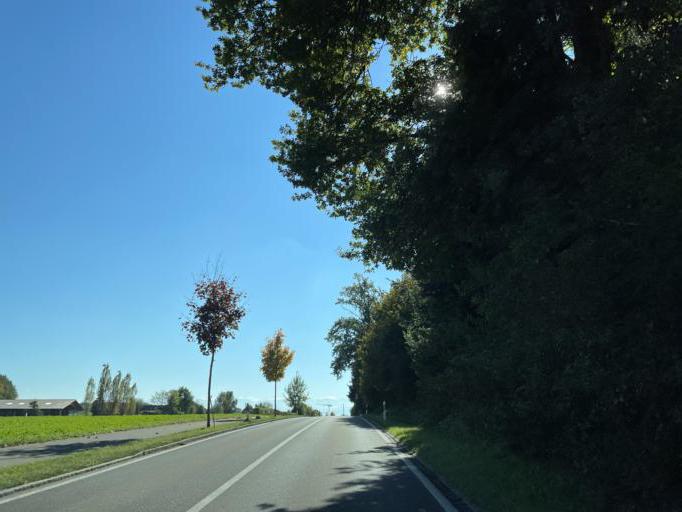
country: CH
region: Zurich
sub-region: Bezirk Uster
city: Gutenswil
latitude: 47.3966
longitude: 8.7158
